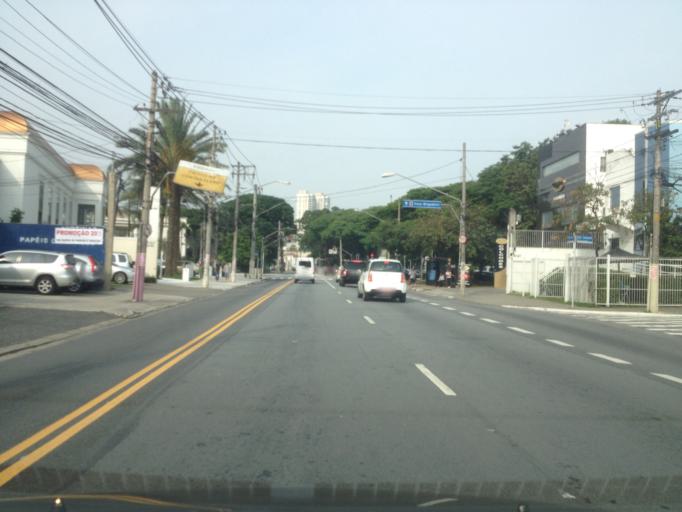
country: BR
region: Sao Paulo
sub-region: Sao Paulo
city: Sao Paulo
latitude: -23.5800
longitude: -46.6630
